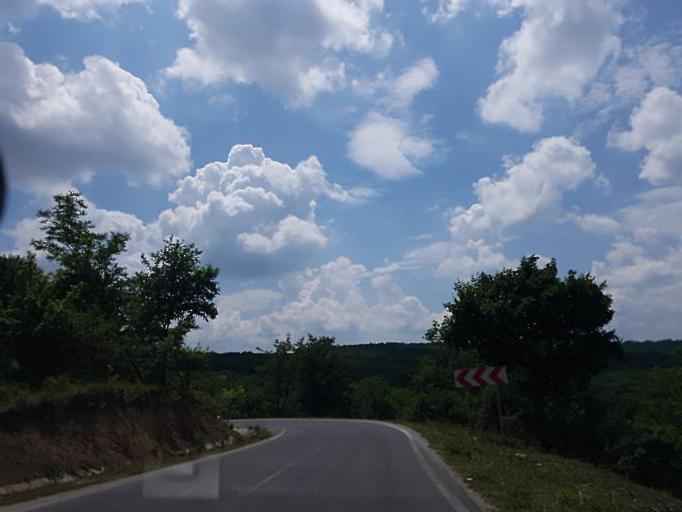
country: RO
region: Sibiu
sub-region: Comuna Seica Mica
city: Seica Mica
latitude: 46.0421
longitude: 24.1563
